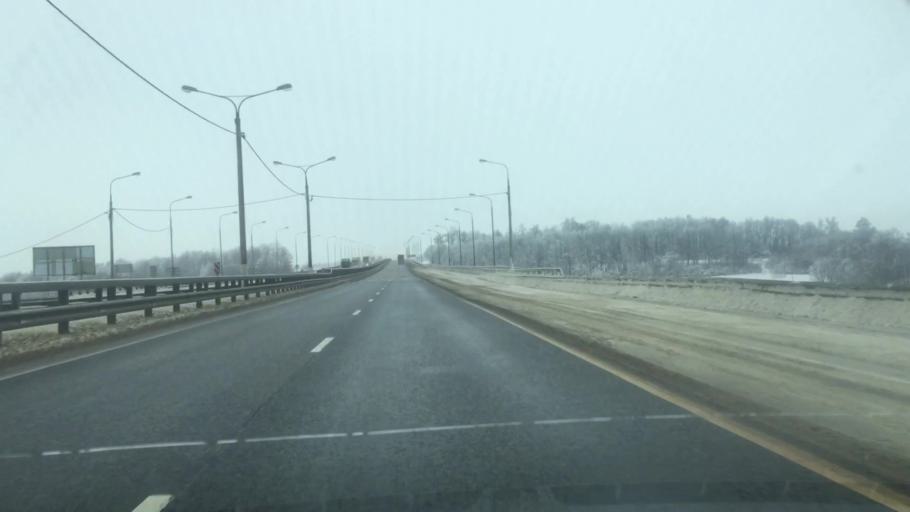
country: RU
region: Lipetsk
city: Stanovoye
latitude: 52.7966
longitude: 38.3215
